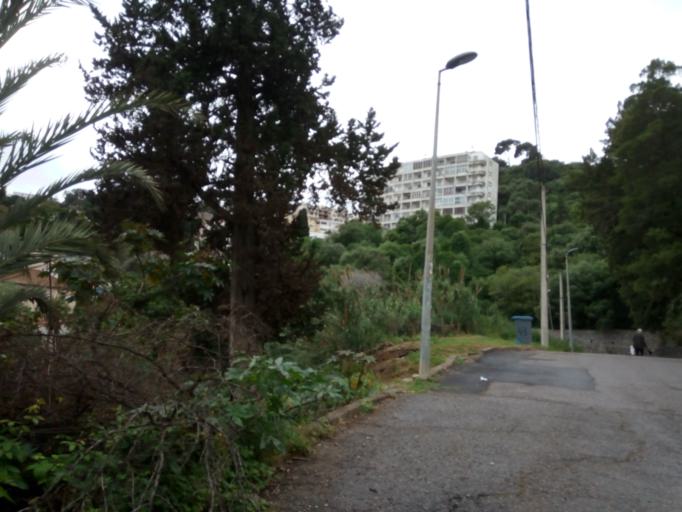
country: DZ
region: Alger
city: Algiers
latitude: 36.7643
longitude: 3.0412
